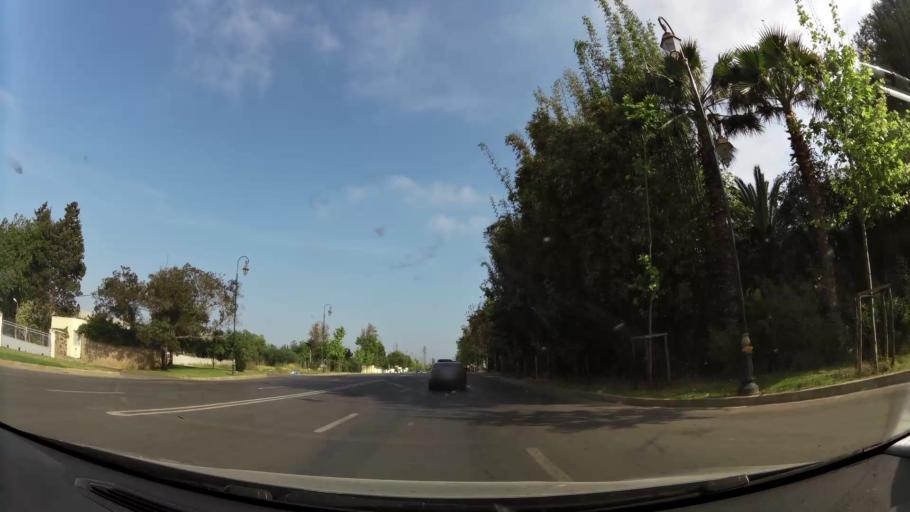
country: MA
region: Rabat-Sale-Zemmour-Zaer
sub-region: Rabat
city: Rabat
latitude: 33.9462
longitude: -6.8100
